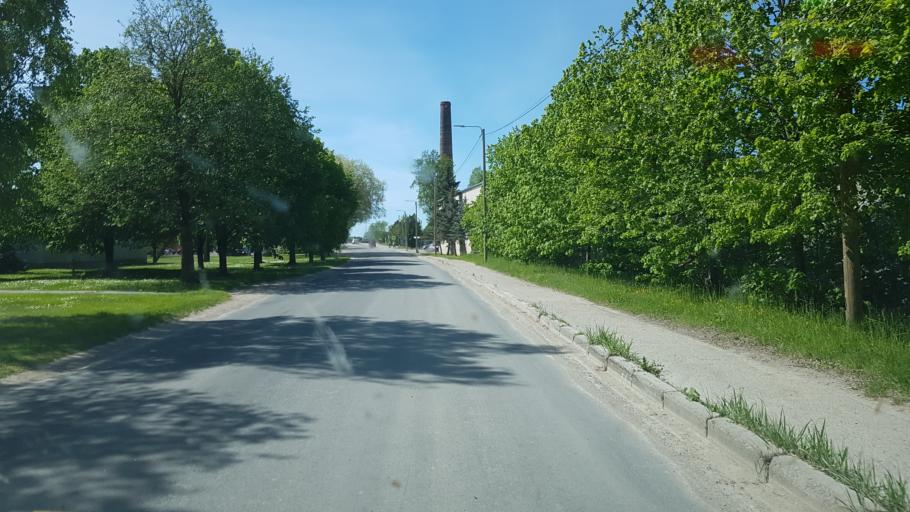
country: EE
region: Saare
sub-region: Kuressaare linn
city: Kuressaare
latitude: 58.2706
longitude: 22.4927
